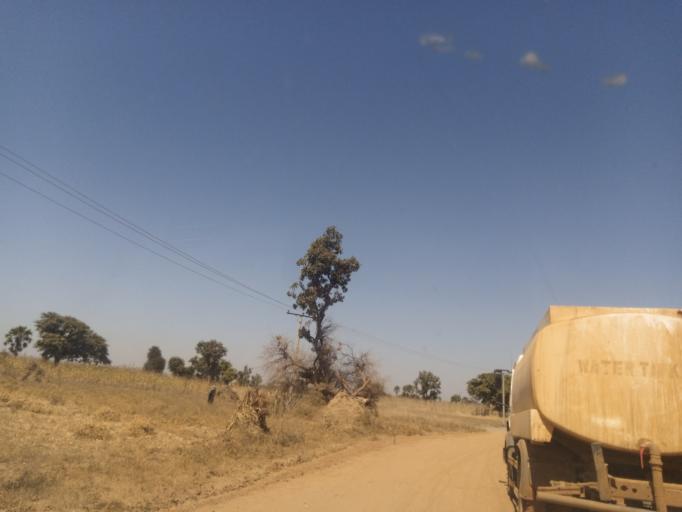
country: NG
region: Adamawa
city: Yola
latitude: 9.2881
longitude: 12.8851
